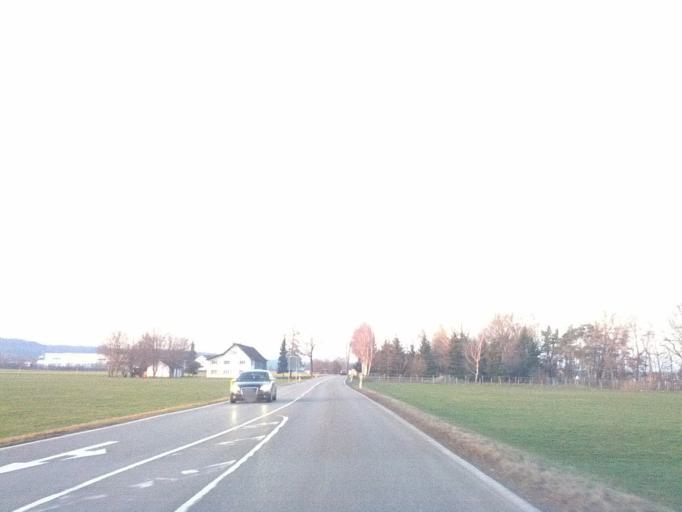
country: DE
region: Baden-Wuerttemberg
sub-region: Tuebingen Region
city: Aitrach
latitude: 47.9260
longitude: 10.1004
